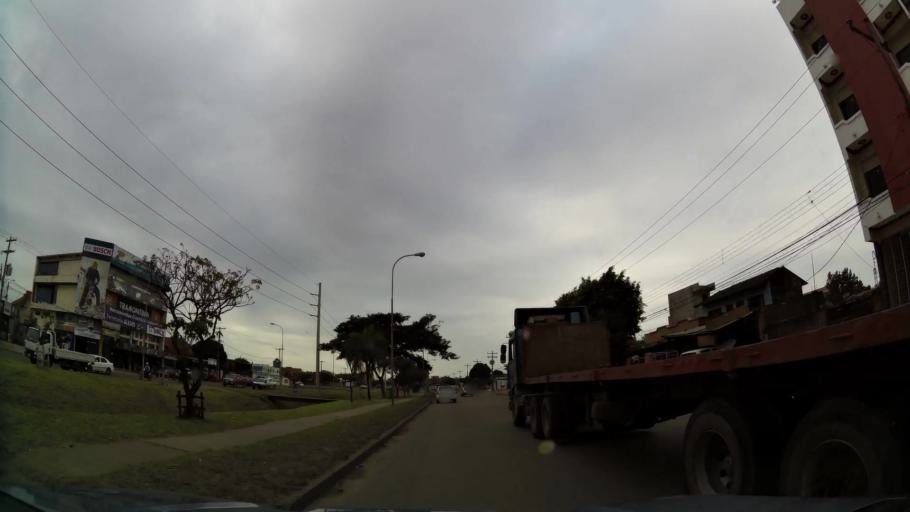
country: BO
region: Santa Cruz
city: Santa Cruz de la Sierra
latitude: -17.7966
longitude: -63.1496
